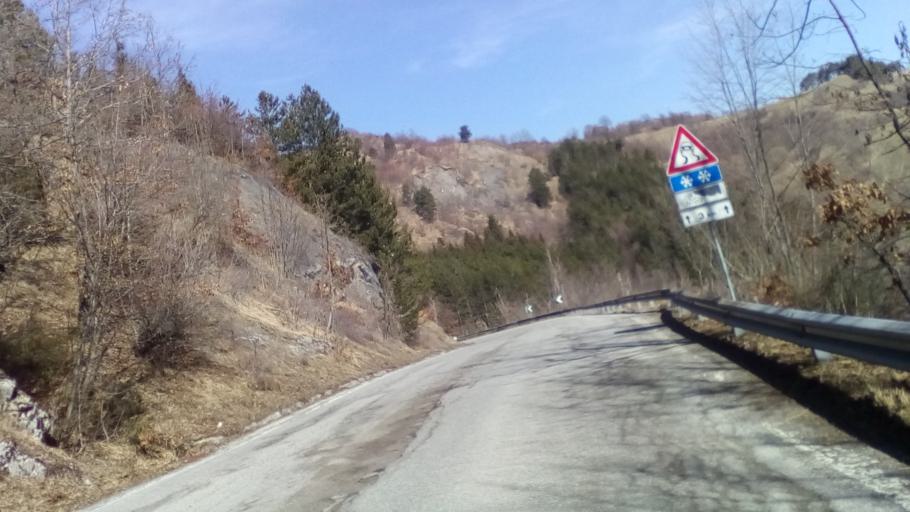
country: IT
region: Emilia-Romagna
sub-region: Provincia di Modena
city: Riolunato
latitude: 44.2356
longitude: 10.6257
